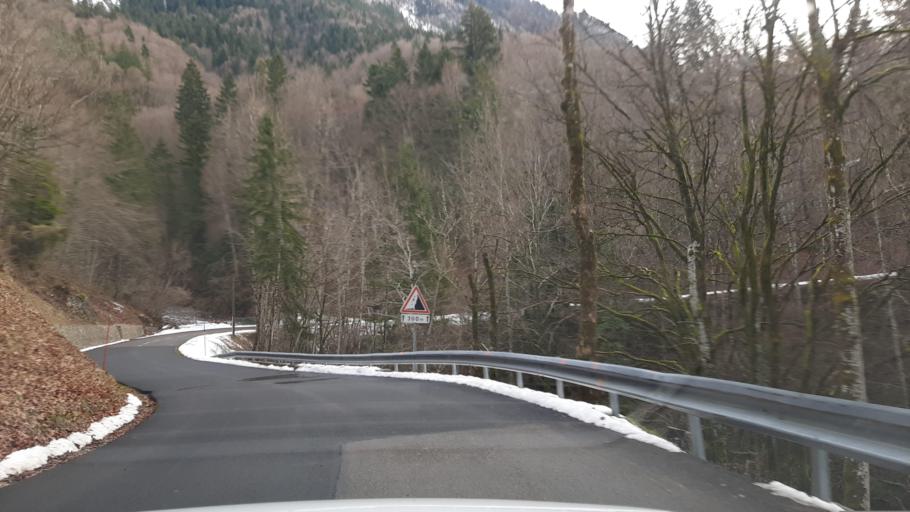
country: FR
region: Rhone-Alpes
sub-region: Departement de la Haute-Savoie
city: Cusy
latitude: 45.6679
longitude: 6.1025
